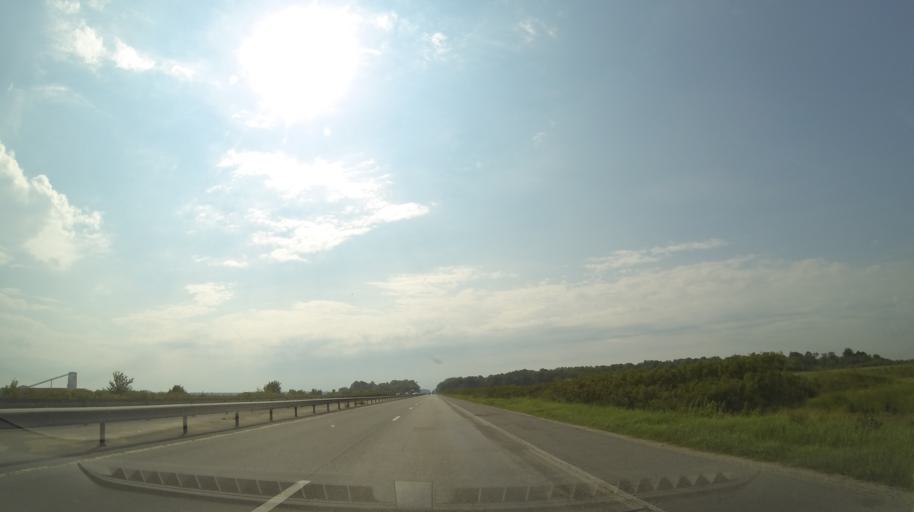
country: RO
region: Giurgiu
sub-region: Comuna Vanatorii Mici
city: Vanatorii Mari
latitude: 44.5281
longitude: 25.5391
